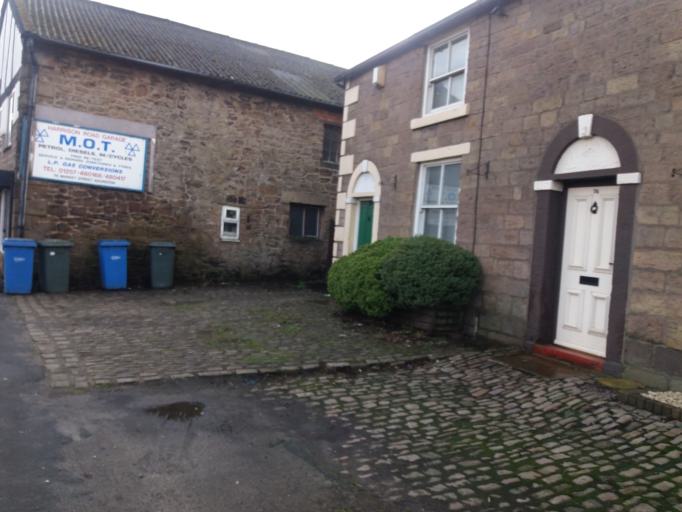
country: GB
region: England
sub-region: Lancashire
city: Adlington
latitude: 53.6096
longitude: -2.6046
